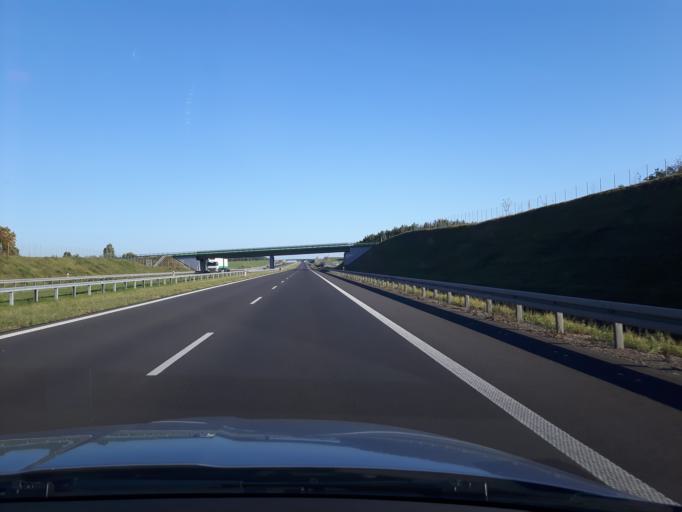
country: PL
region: Warmian-Masurian Voivodeship
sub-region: Powiat nidzicki
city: Nidzica
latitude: 53.3109
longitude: 20.4377
